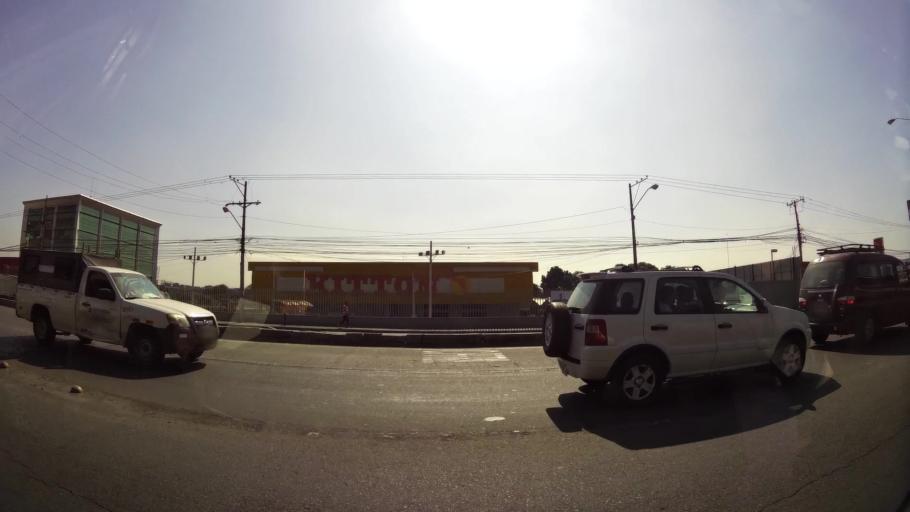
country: EC
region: Guayas
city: Guayaquil
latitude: -2.1753
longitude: -79.9132
